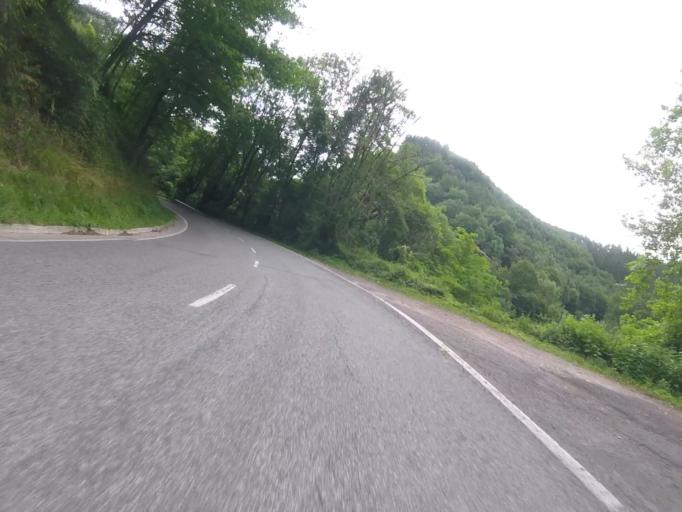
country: ES
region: Navarre
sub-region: Provincia de Navarra
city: Zubieta
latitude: 43.1236
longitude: -1.7527
